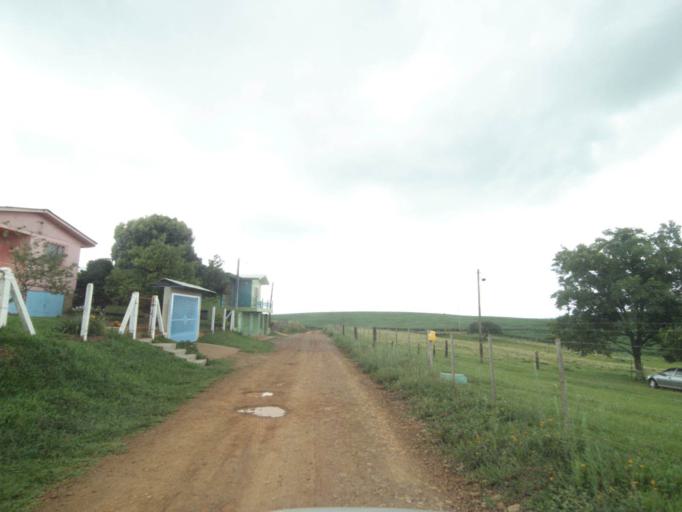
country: BR
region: Rio Grande do Sul
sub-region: Lagoa Vermelha
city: Lagoa Vermelha
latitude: -28.2088
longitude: -51.5521
